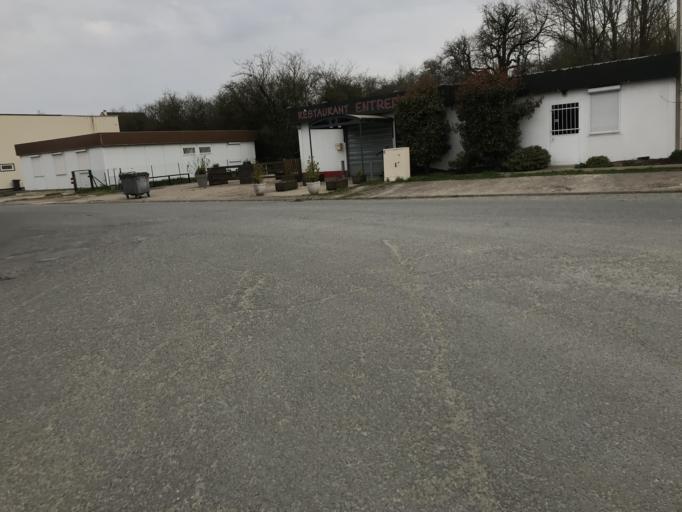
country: FR
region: Ile-de-France
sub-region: Departement de l'Essonne
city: Limours
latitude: 48.6467
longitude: 2.0599
